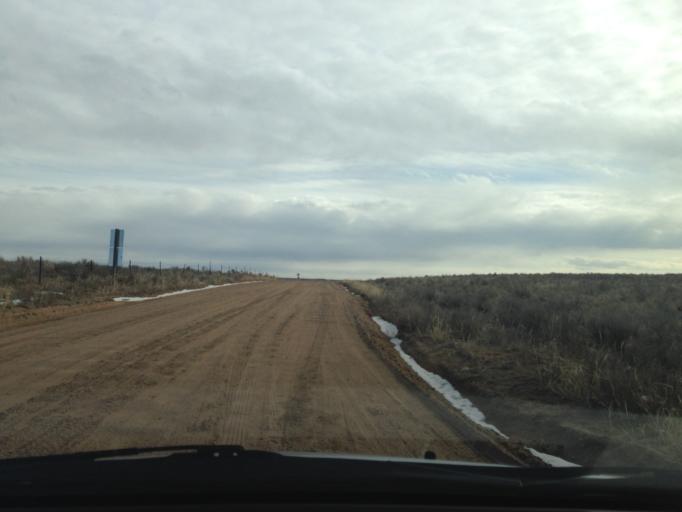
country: US
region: Colorado
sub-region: Weld County
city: Keenesburg
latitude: 40.2833
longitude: -104.2067
